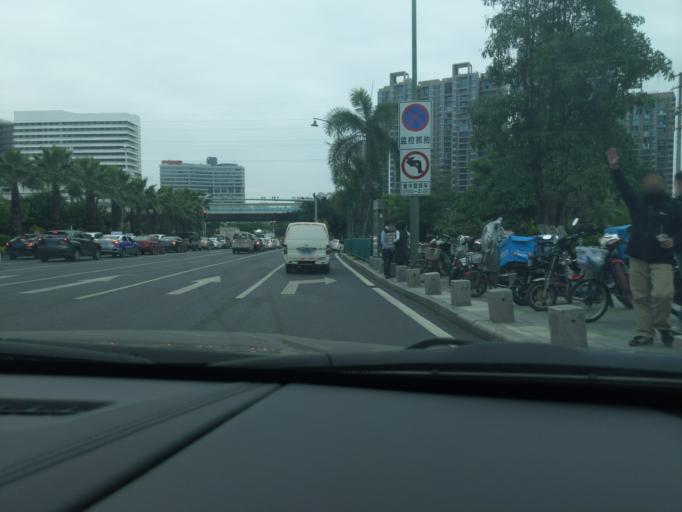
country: CN
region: Fujian
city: Liuwudian
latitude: 24.5077
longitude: 118.1711
